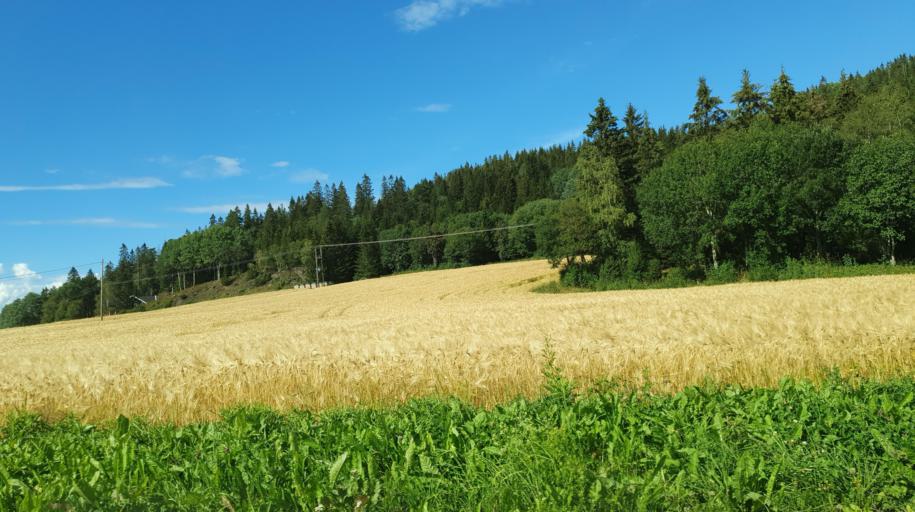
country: NO
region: Nord-Trondelag
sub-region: Levanger
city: Levanger
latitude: 63.6980
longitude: 11.2575
